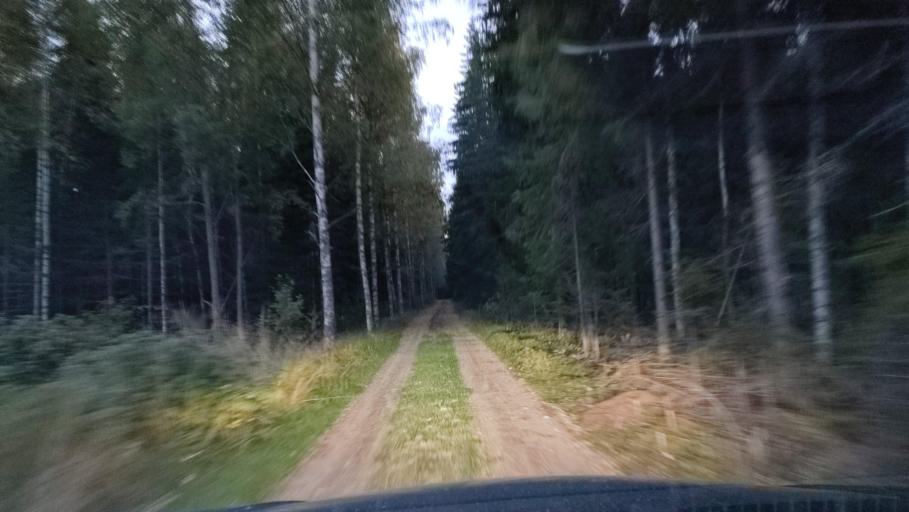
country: FI
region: Ostrobothnia
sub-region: Sydosterbotten
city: Kristinestad
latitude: 62.3385
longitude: 21.3588
